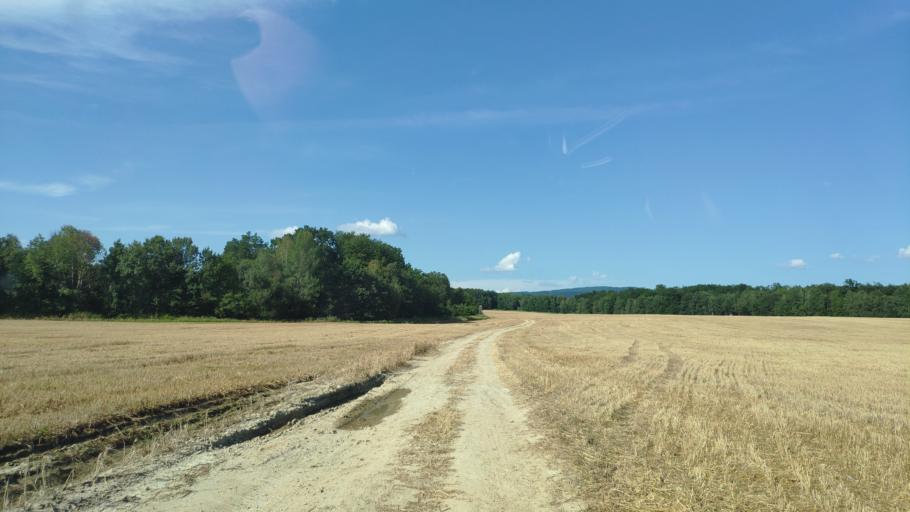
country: SK
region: Presovsky
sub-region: Okres Presov
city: Presov
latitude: 48.9147
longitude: 21.2988
